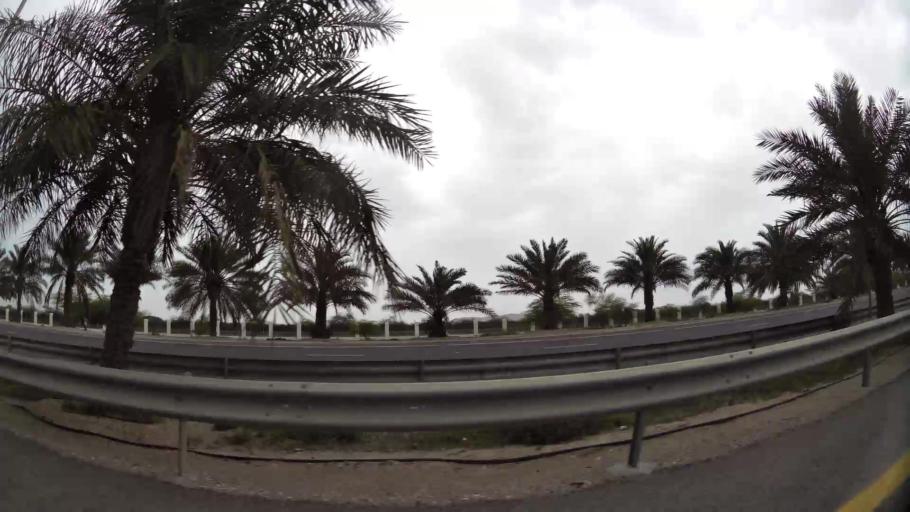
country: BH
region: Central Governorate
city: Dar Kulayb
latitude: 26.0616
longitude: 50.5209
